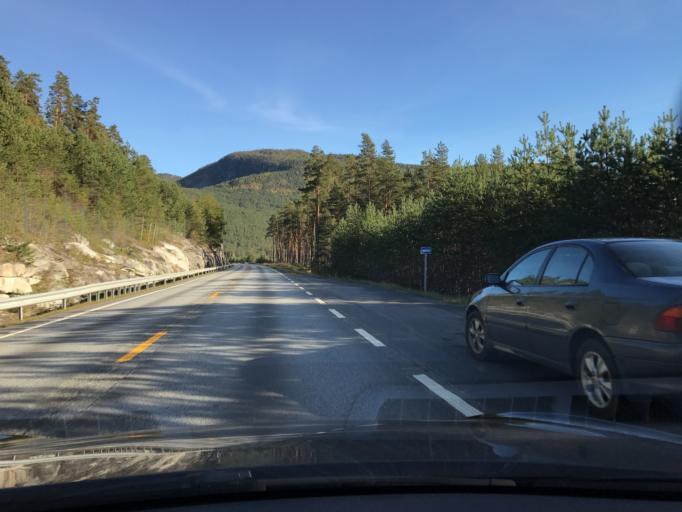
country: NO
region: Sogn og Fjordane
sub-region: Sogndal
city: Sogndalsfjora
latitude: 61.1818
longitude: 7.2792
